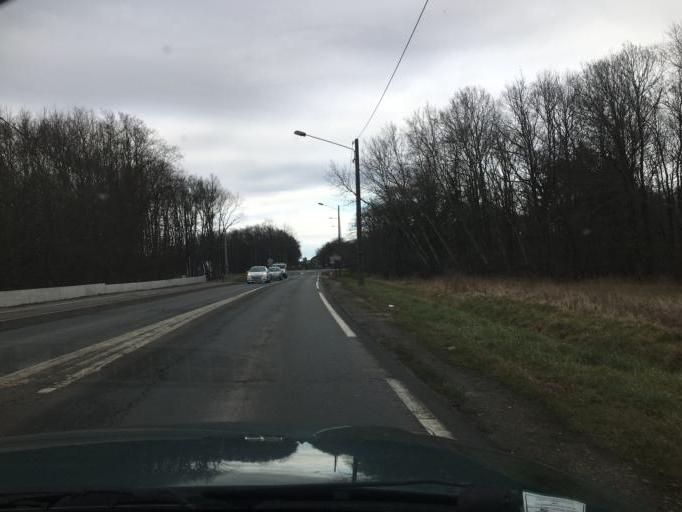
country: FR
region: Centre
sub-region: Departement du Loiret
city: Fleury-les-Aubrais
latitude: 47.9519
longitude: 1.9215
